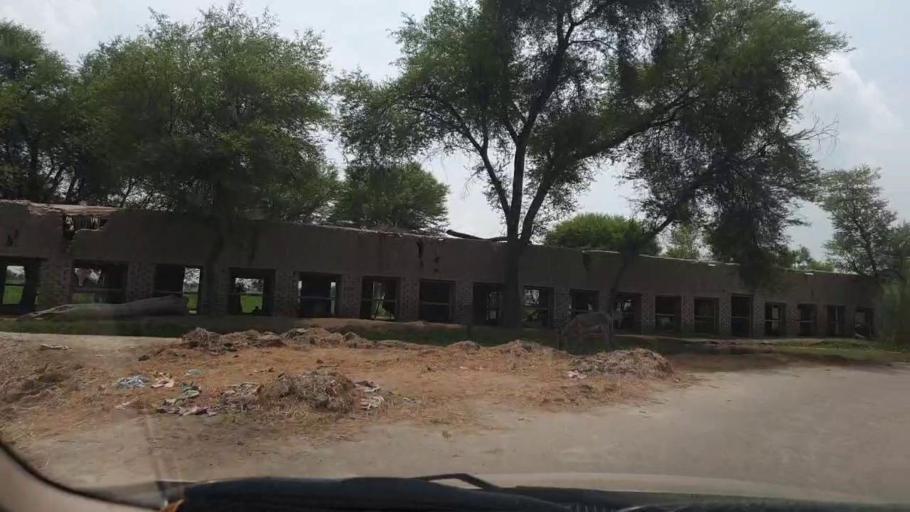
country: PK
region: Sindh
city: Larkana
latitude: 27.6247
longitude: 68.1521
